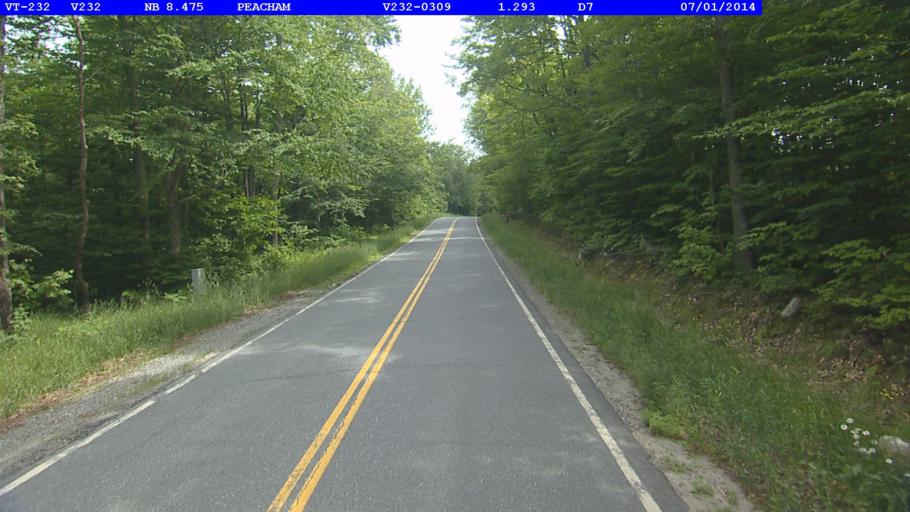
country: US
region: Vermont
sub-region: Caledonia County
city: Hardwick
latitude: 44.3135
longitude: -72.2998
